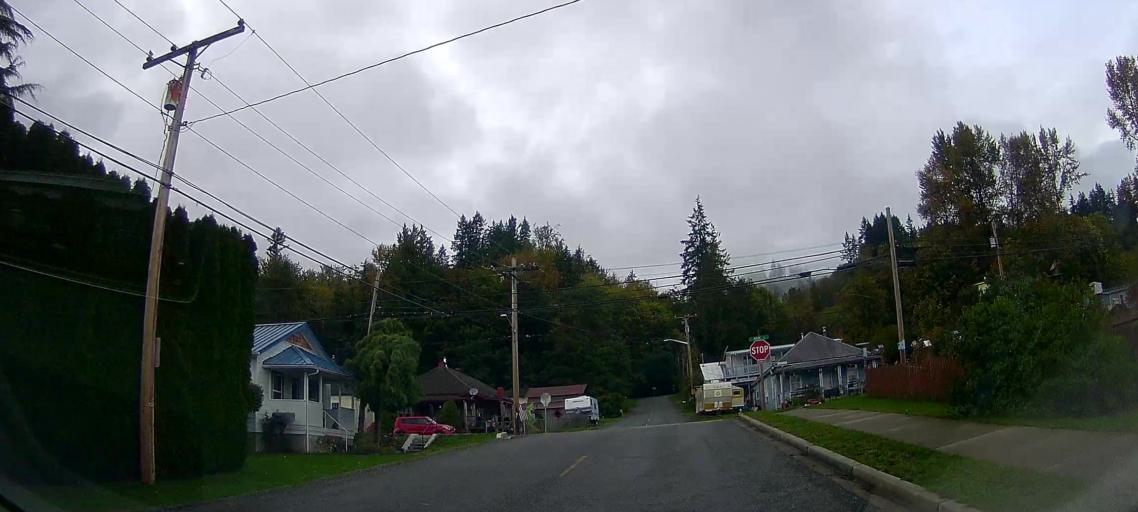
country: US
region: Washington
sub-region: Snohomish County
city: Darrington
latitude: 48.5379
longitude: -121.7584
